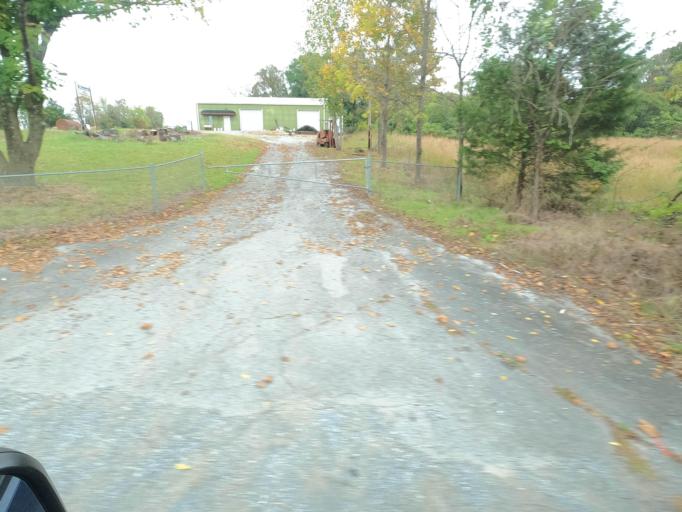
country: US
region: Tennessee
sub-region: Washington County
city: Jonesborough
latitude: 36.2537
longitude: -82.5914
